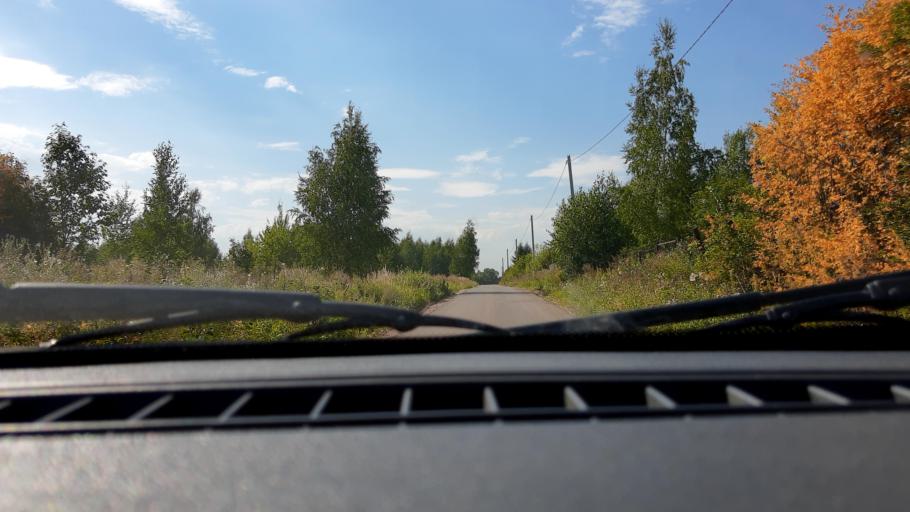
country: RU
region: Bashkortostan
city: Ufa
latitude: 54.8484
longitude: 56.1612
